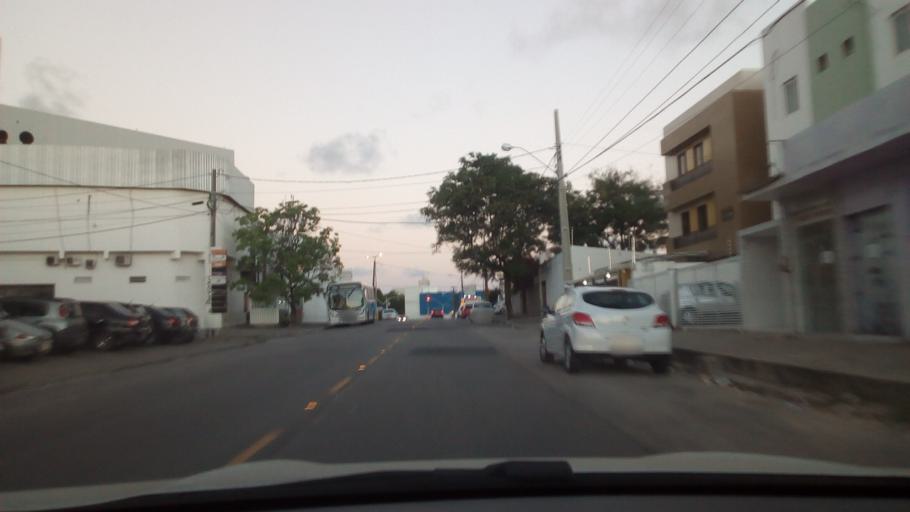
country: BR
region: Paraiba
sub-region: Joao Pessoa
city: Joao Pessoa
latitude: -7.1496
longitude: -34.8435
